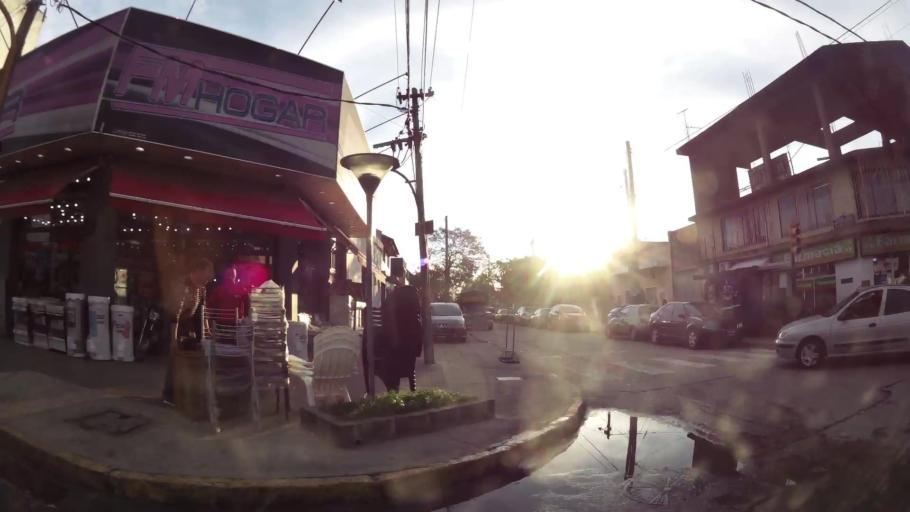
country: AR
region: Buenos Aires
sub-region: Partido de Almirante Brown
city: Adrogue
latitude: -34.7697
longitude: -58.3554
